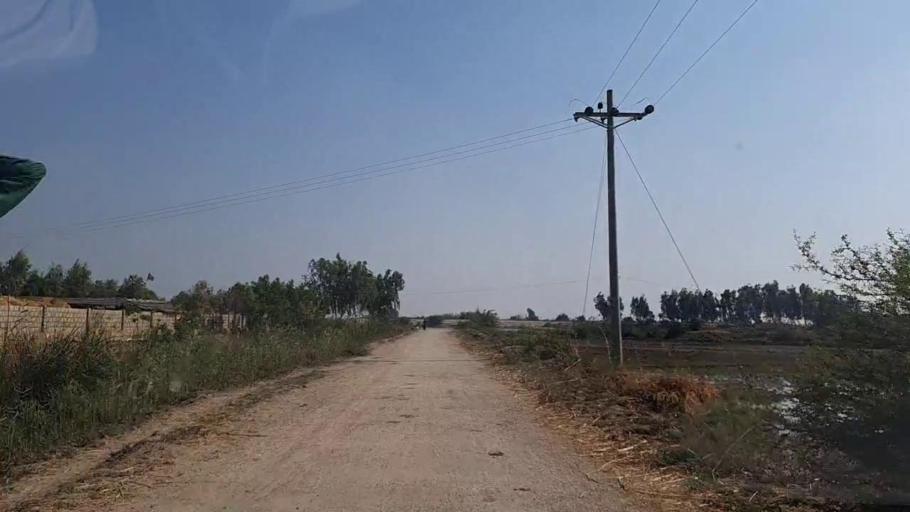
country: PK
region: Sindh
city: Thatta
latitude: 24.7964
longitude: 67.9766
